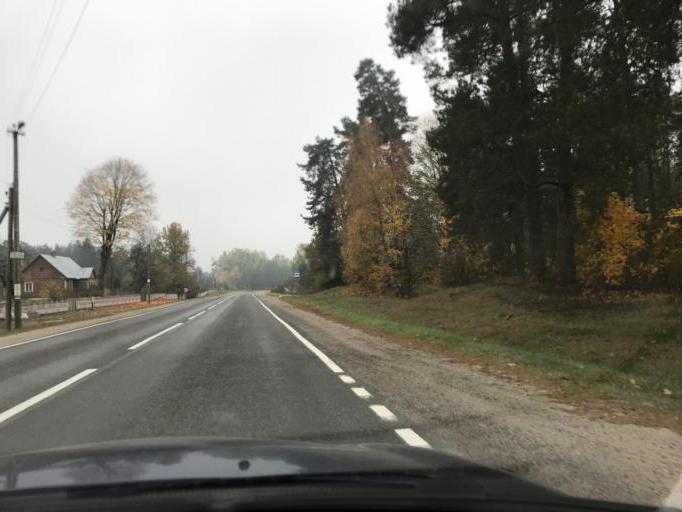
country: BY
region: Grodnenskaya
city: Hrodna
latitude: 53.8390
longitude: 23.8937
